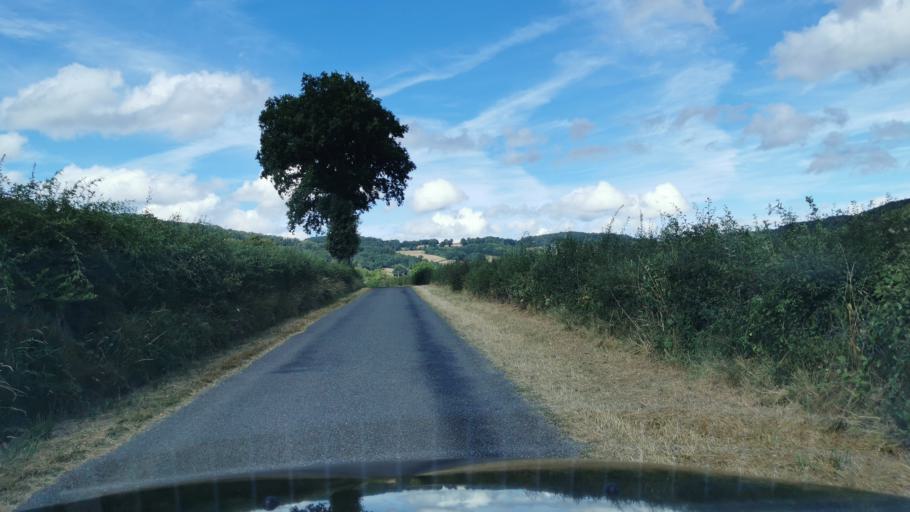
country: FR
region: Bourgogne
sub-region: Departement de Saone-et-Loire
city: Marmagne
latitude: 46.8623
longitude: 4.3108
